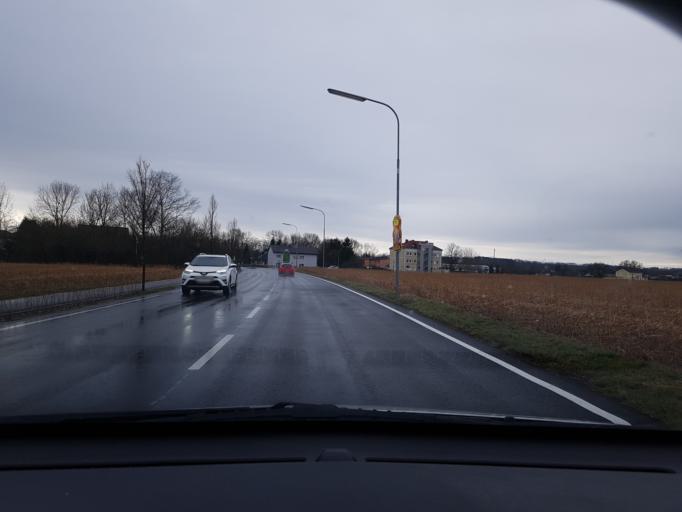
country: AT
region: Upper Austria
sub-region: Politischer Bezirk Linz-Land
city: Traun
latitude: 48.2175
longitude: 14.2188
